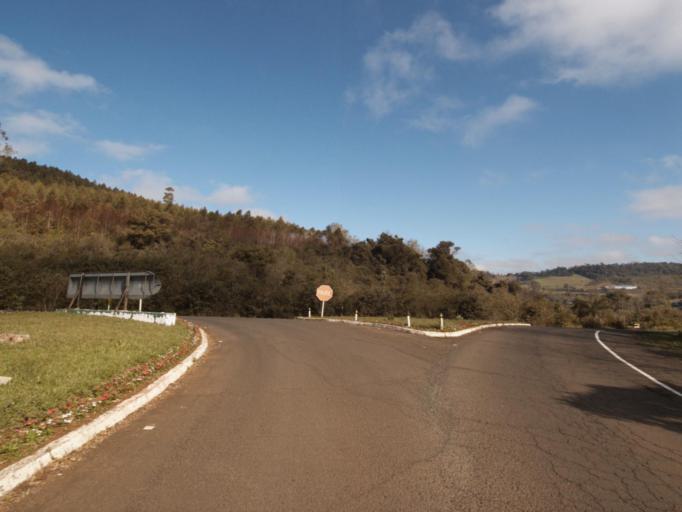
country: BR
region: Rio Grande do Sul
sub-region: Frederico Westphalen
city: Frederico Westphalen
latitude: -27.0798
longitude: -53.2244
